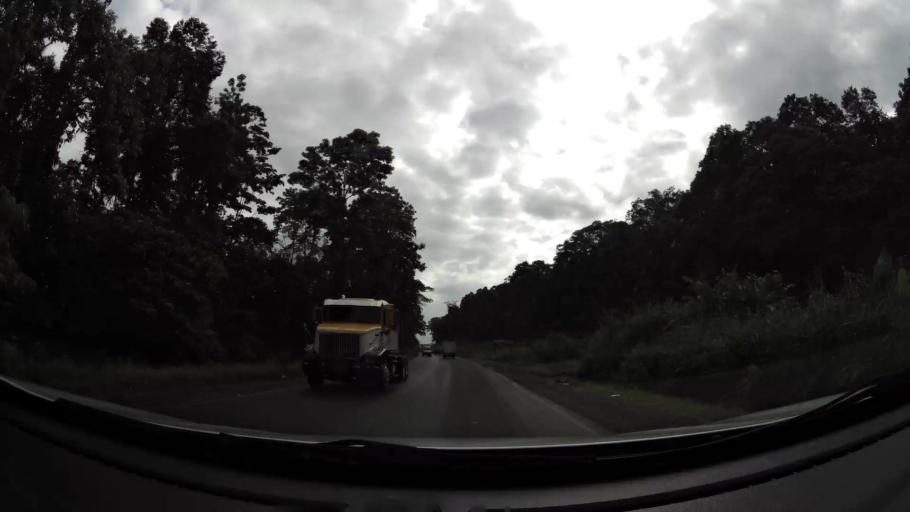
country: CR
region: Limon
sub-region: Canton de Siquirres
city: Siquirres
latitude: 10.1022
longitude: -83.5249
